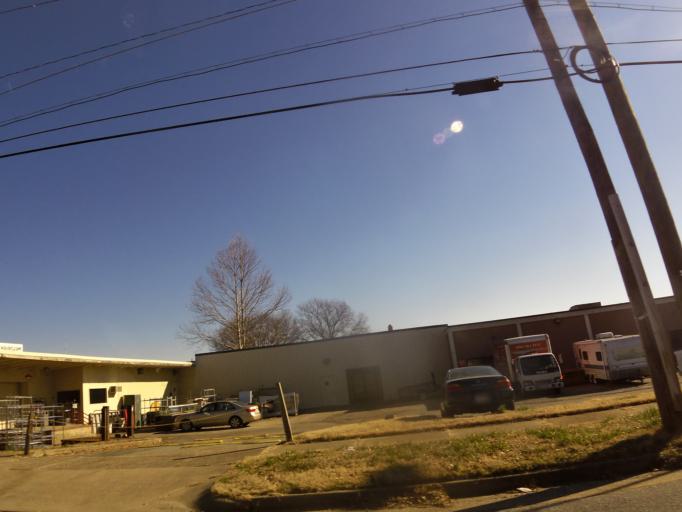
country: US
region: Virginia
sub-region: City of Richmond
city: Richmond
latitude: 37.5604
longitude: -77.4439
